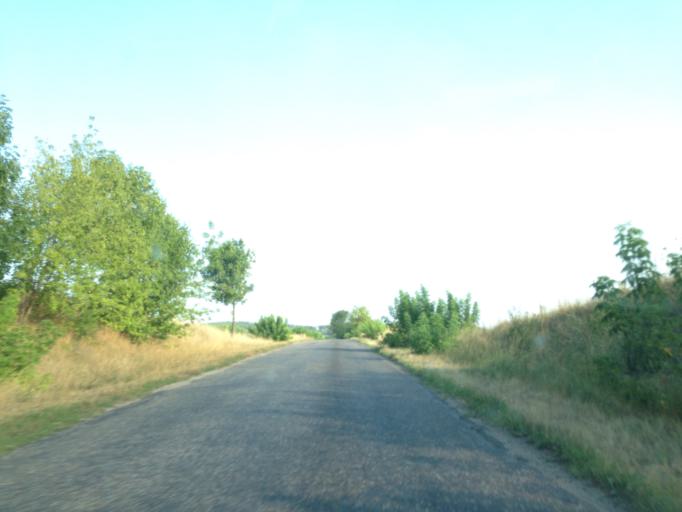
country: PL
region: Warmian-Masurian Voivodeship
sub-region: Powiat nowomiejski
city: Biskupiec
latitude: 53.4655
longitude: 19.2676
